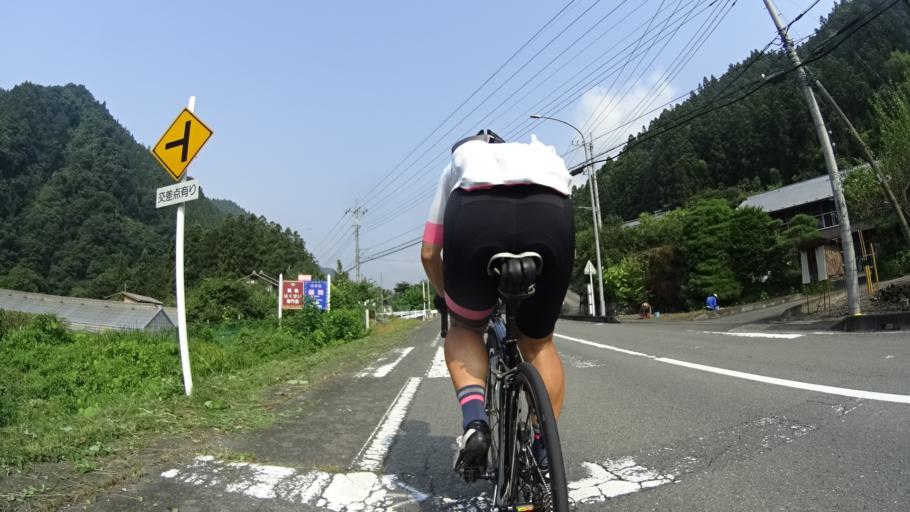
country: JP
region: Saitama
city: Chichibu
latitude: 36.0254
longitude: 138.9528
